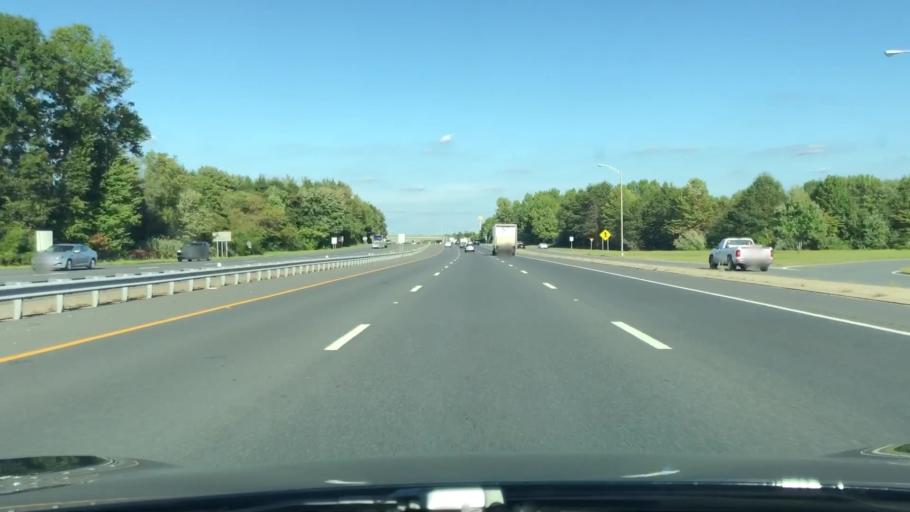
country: US
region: New Jersey
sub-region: Gloucester County
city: Paulsboro
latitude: 39.8178
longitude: -75.2470
